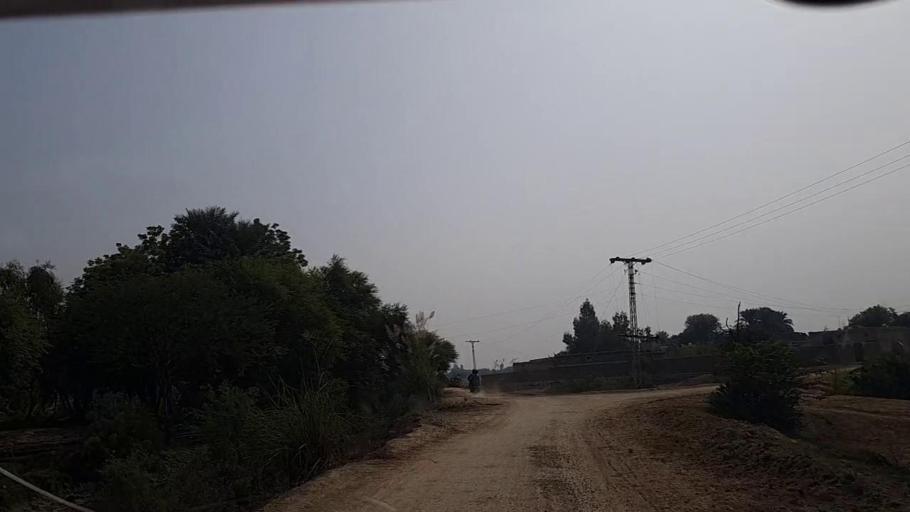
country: PK
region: Sindh
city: Garhi Yasin
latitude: 27.9231
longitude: 68.5697
